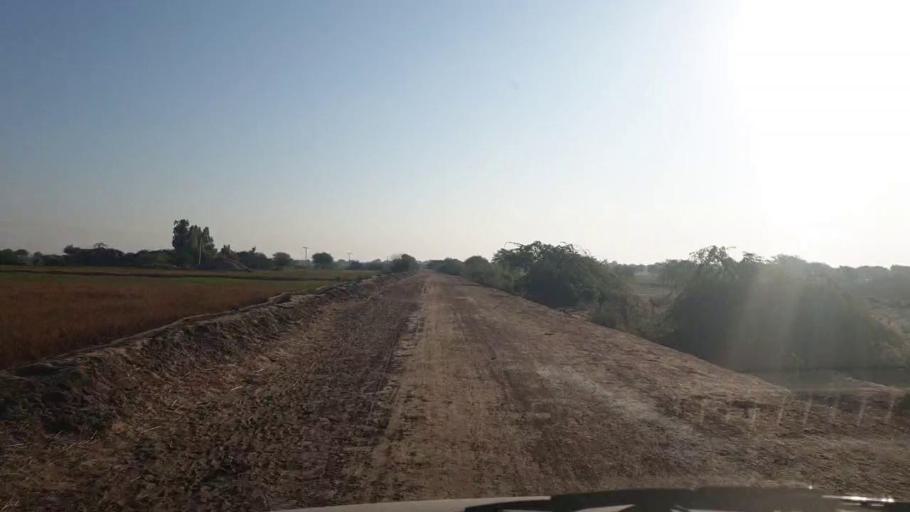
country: PK
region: Sindh
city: Talhar
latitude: 24.8082
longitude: 68.8417
